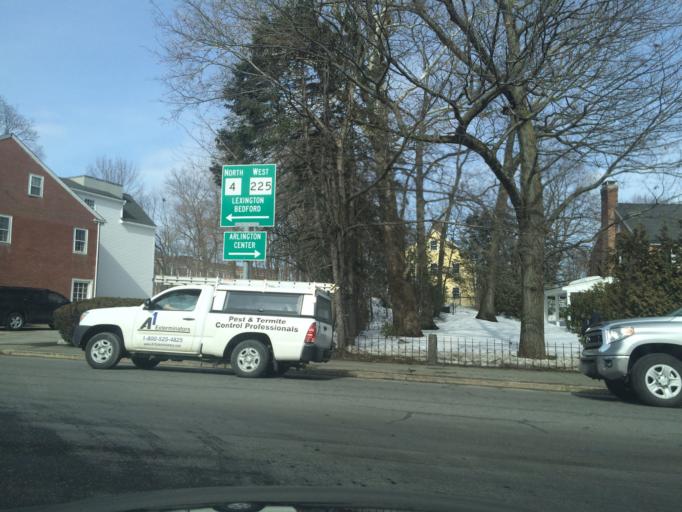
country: US
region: Massachusetts
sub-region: Middlesex County
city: Lexington
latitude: 42.4286
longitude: -71.2066
